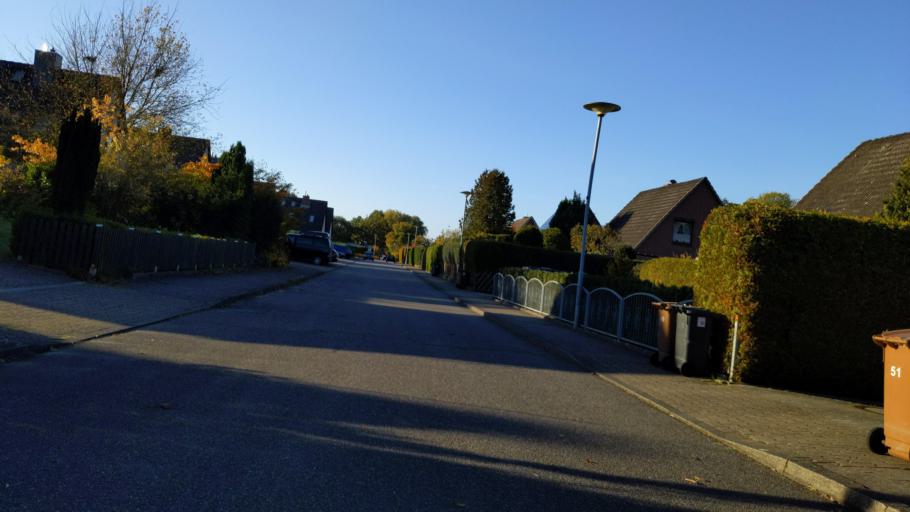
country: DE
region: Schleswig-Holstein
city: Gross Gronau
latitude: 53.8290
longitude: 10.7331
